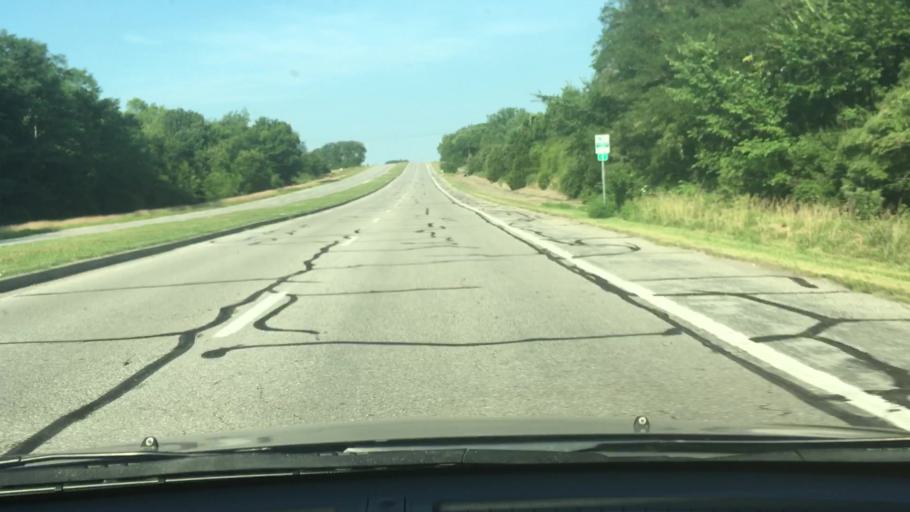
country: US
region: Missouri
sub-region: Jackson County
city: Grandview
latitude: 38.8894
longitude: -94.4614
